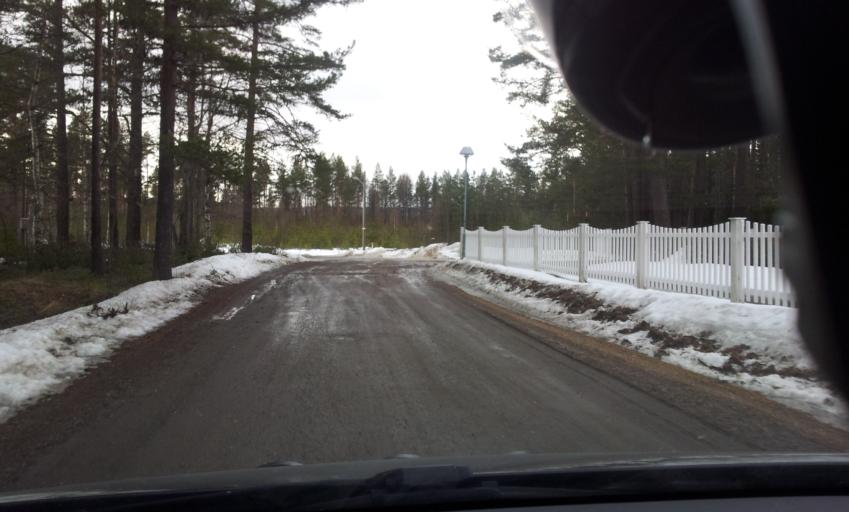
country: SE
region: Vaesternorrland
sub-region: Ange Kommun
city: Ange
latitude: 62.1878
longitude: 15.6597
